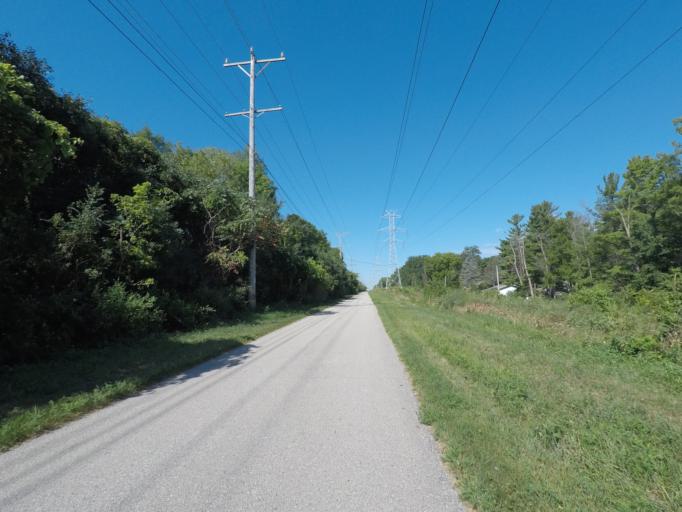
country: US
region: Wisconsin
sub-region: Waukesha County
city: Elm Grove
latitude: 43.0103
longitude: -88.0710
